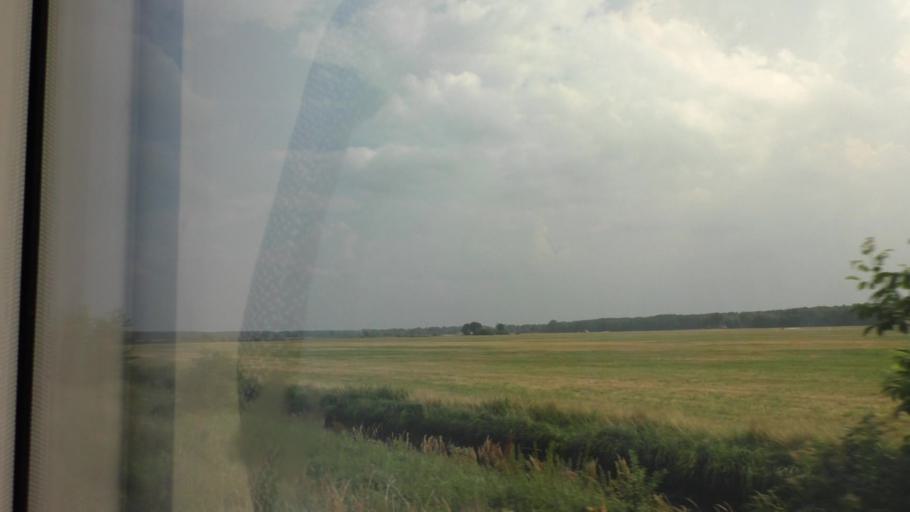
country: DE
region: Brandenburg
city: Spreenhagen
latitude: 52.2868
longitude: 13.8034
